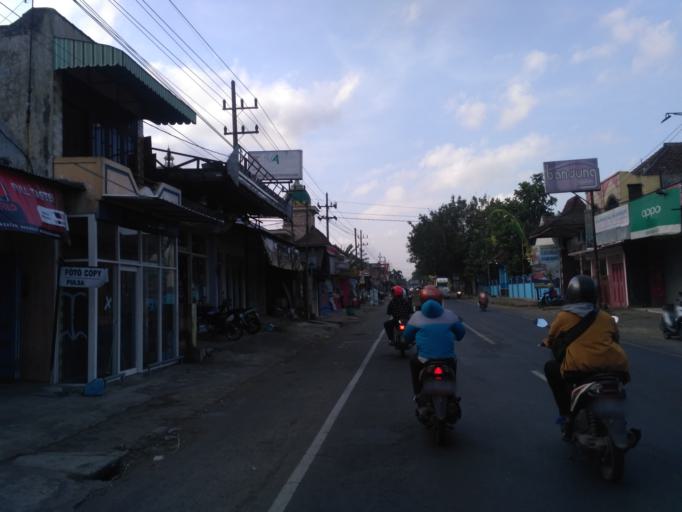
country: ID
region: East Java
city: Pakisaji
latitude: -8.0659
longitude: 112.5987
